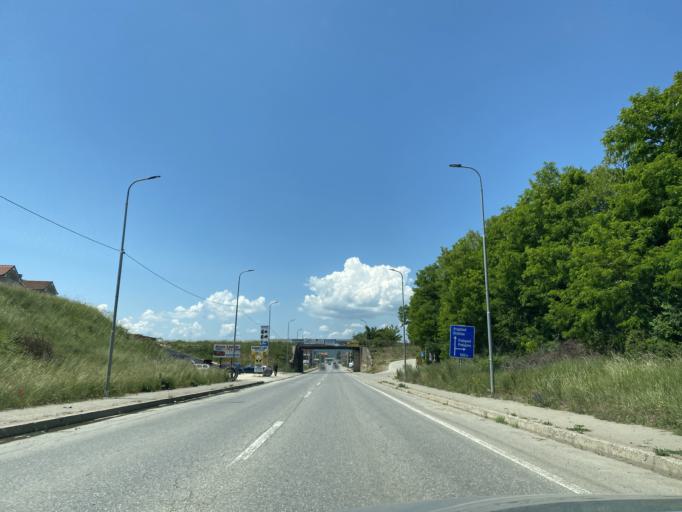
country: XK
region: Pristina
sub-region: Podujevo
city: Podujeva
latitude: 42.8988
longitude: 21.2047
